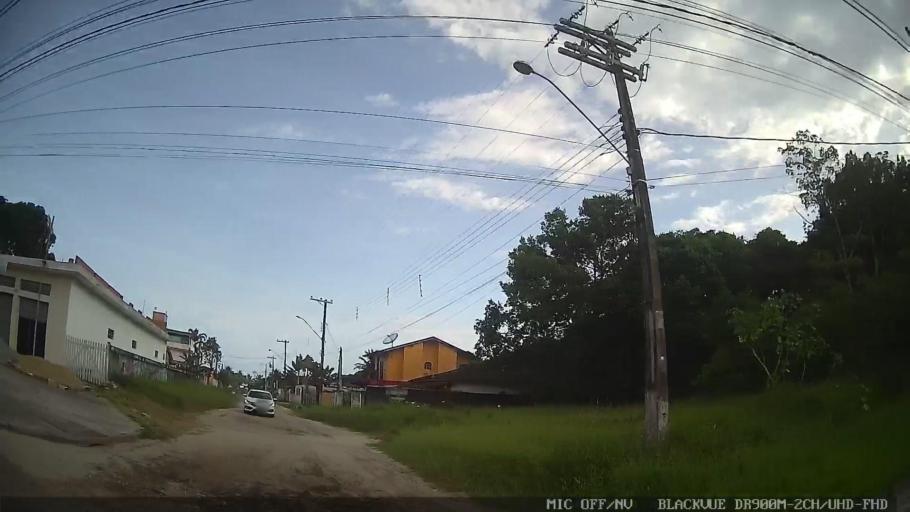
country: BR
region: Sao Paulo
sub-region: Bertioga
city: Bertioga
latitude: -23.8154
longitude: -46.0831
